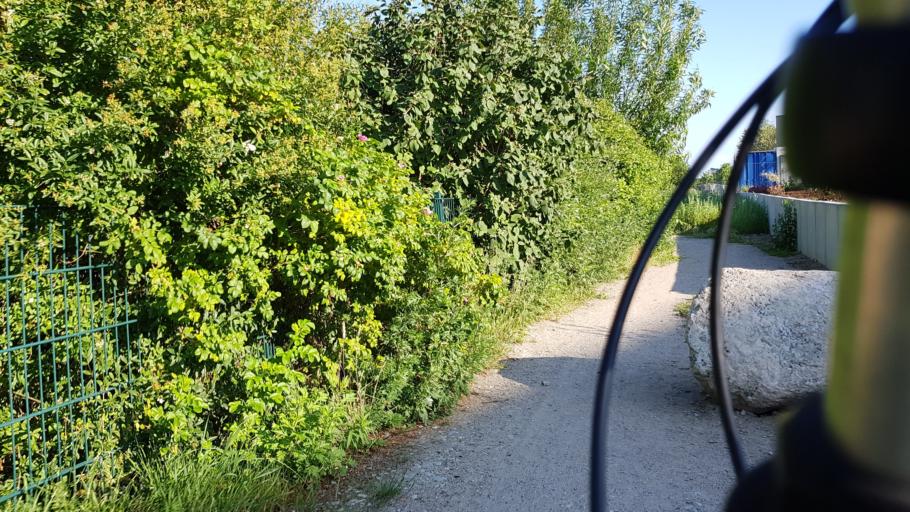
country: DE
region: Mecklenburg-Vorpommern
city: Werdervorstadt
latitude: 53.6328
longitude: 11.4283
